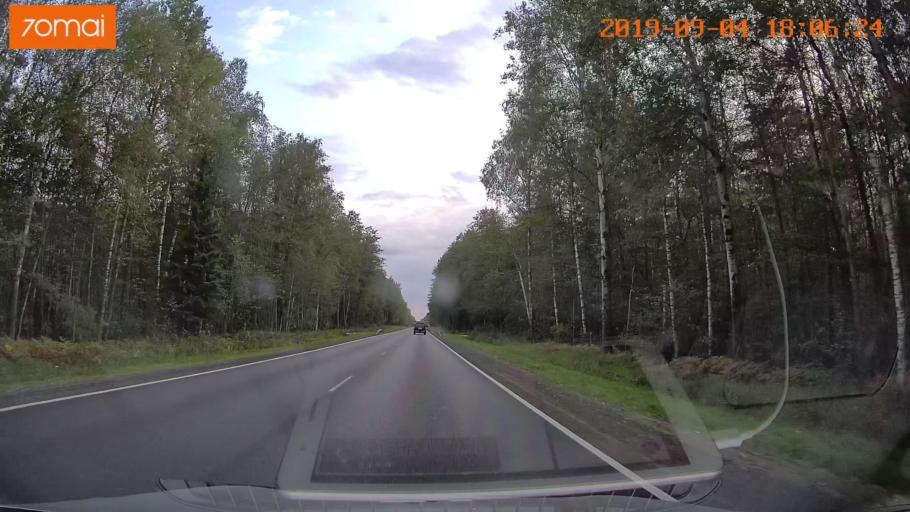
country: RU
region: Moskovskaya
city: Khorlovo
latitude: 55.4315
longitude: 38.8152
